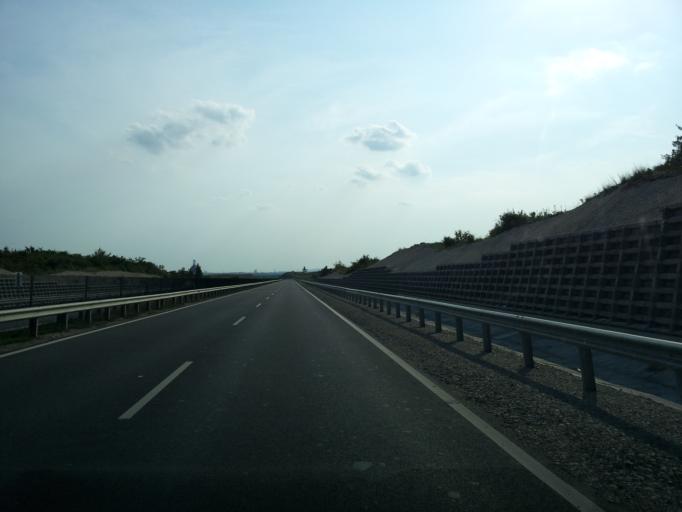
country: HU
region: Veszprem
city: Hajmasker
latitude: 47.1333
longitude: 18.0163
